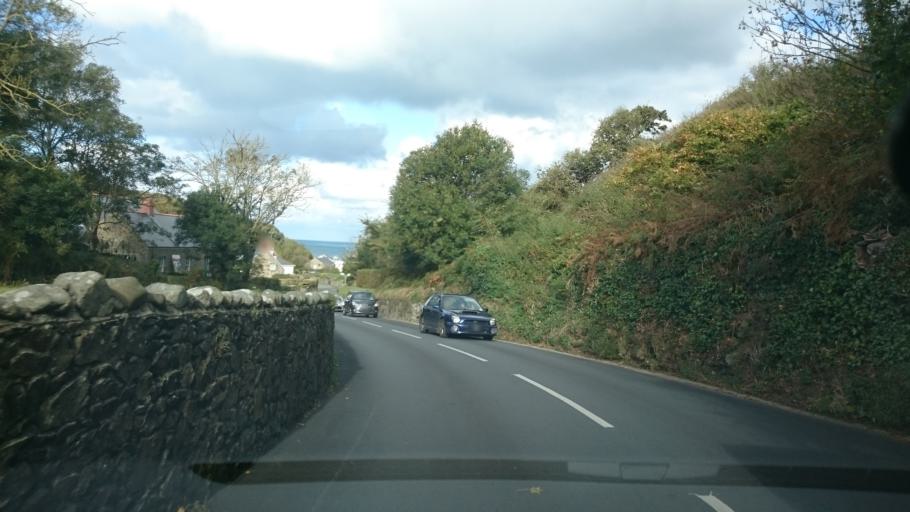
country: GG
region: St Peter Port
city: Saint Peter Port
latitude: 49.4319
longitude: -2.6582
